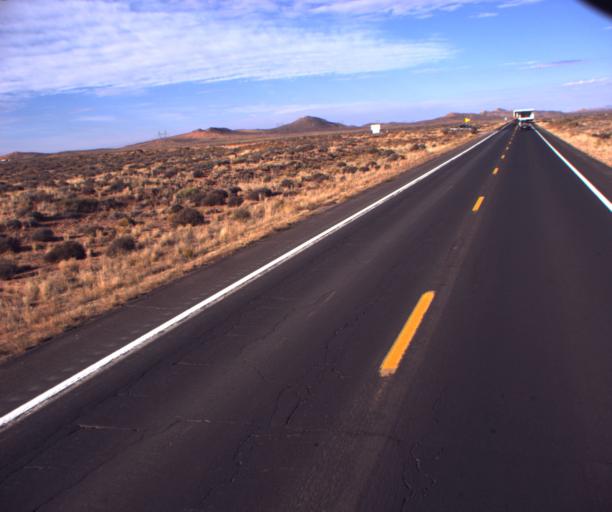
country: US
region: Arizona
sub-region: Apache County
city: Lukachukai
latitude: 36.9632
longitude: -109.4543
